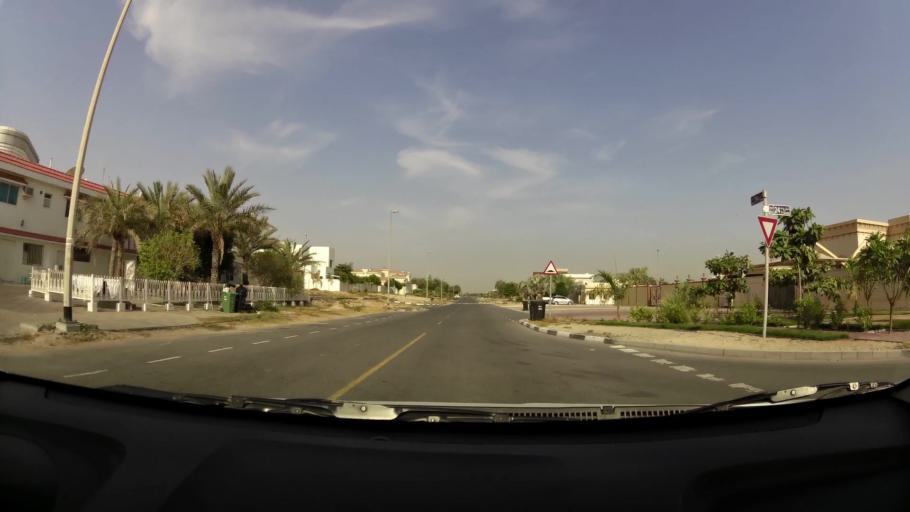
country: AE
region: Ash Shariqah
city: Sharjah
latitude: 25.2465
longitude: 55.4156
